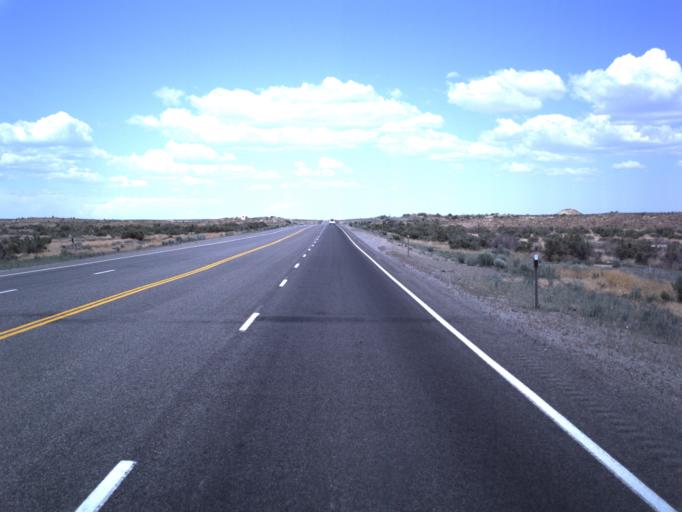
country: US
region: Utah
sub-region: Emery County
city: Huntington
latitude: 39.3831
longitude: -110.9065
